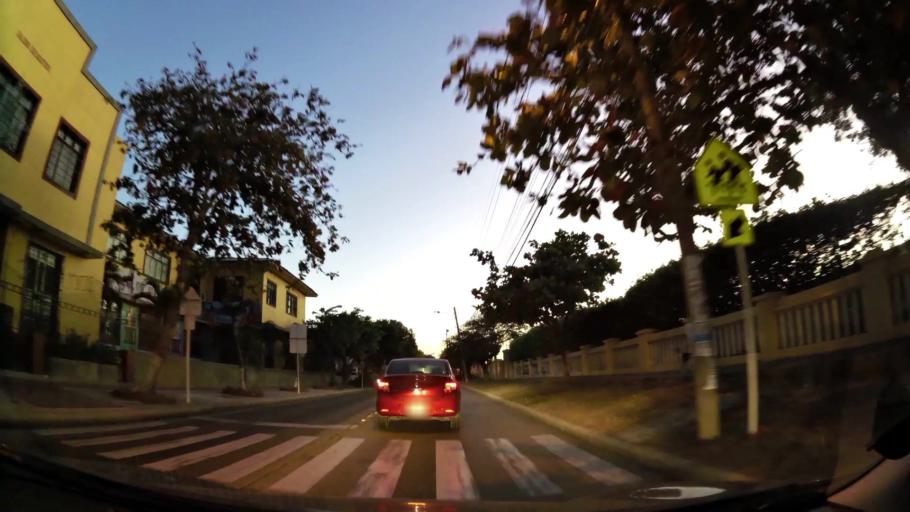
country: CO
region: Atlantico
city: Barranquilla
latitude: 10.9809
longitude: -74.8005
